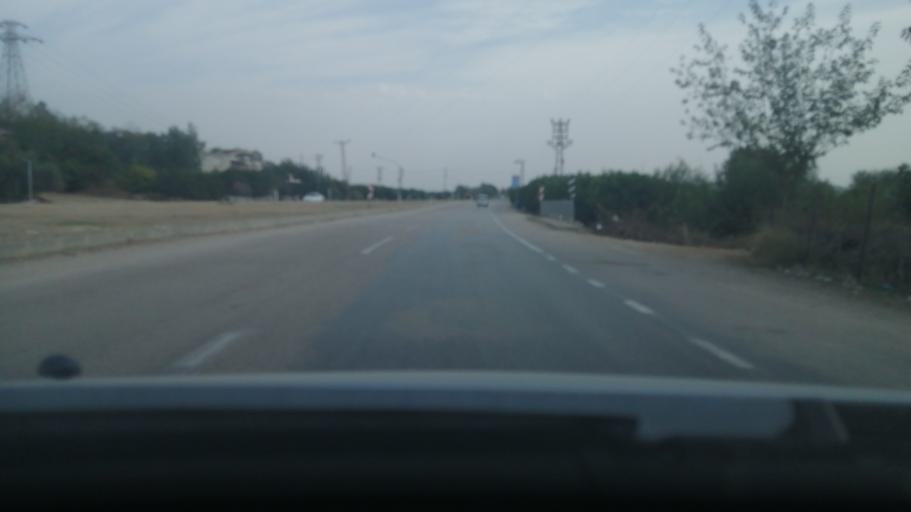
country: TR
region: Adana
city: Kozan
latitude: 37.3799
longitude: 35.8266
